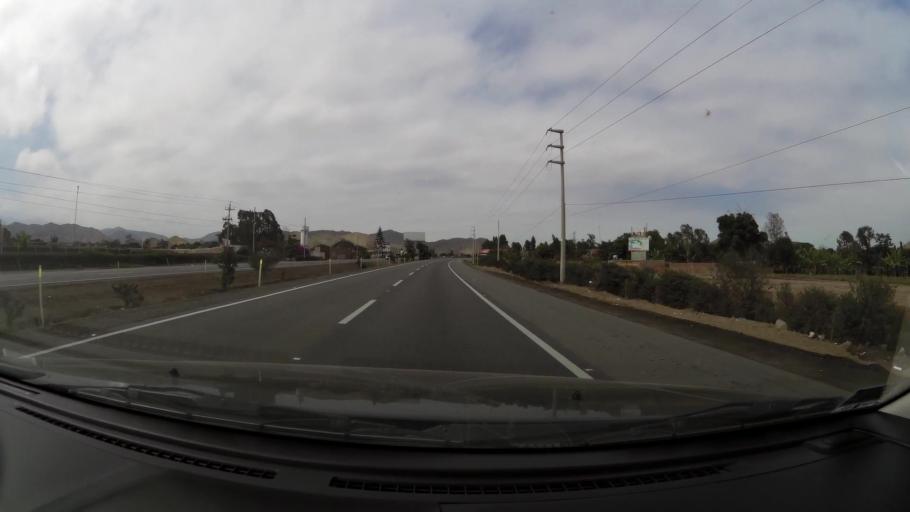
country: PE
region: Lima
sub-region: Provincia de Canete
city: Mala
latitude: -12.7188
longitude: -76.6222
